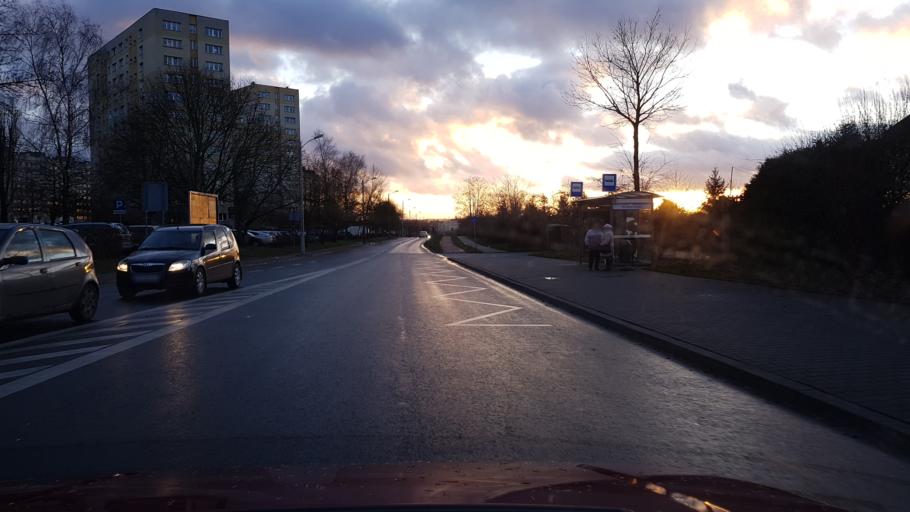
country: PL
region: West Pomeranian Voivodeship
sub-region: Szczecin
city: Szczecin
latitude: 53.4329
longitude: 14.5029
